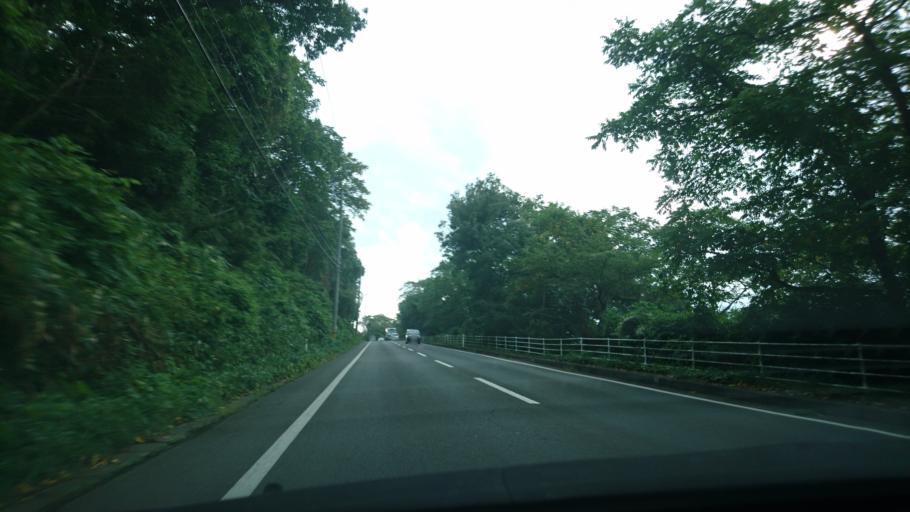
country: JP
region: Iwate
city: Kitakami
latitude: 39.2652
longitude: 141.1256
